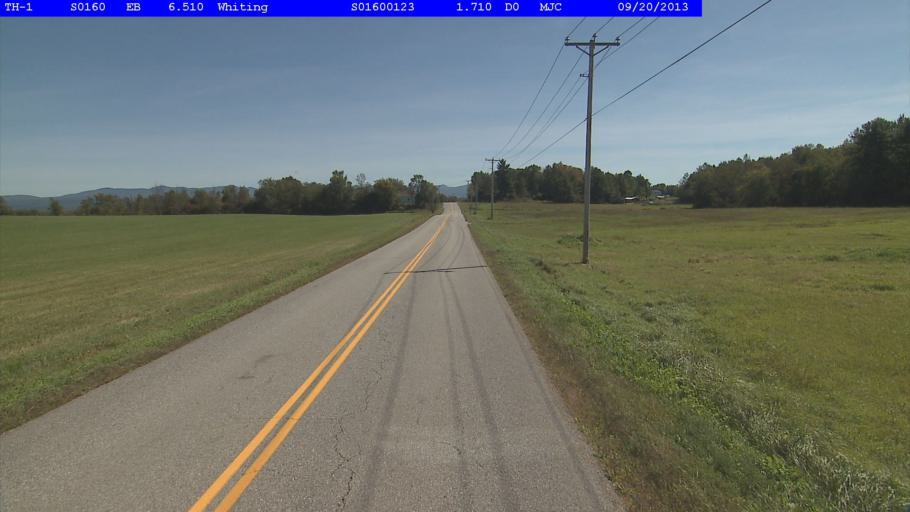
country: US
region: Vermont
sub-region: Rutland County
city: Brandon
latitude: 43.8614
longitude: -73.1922
